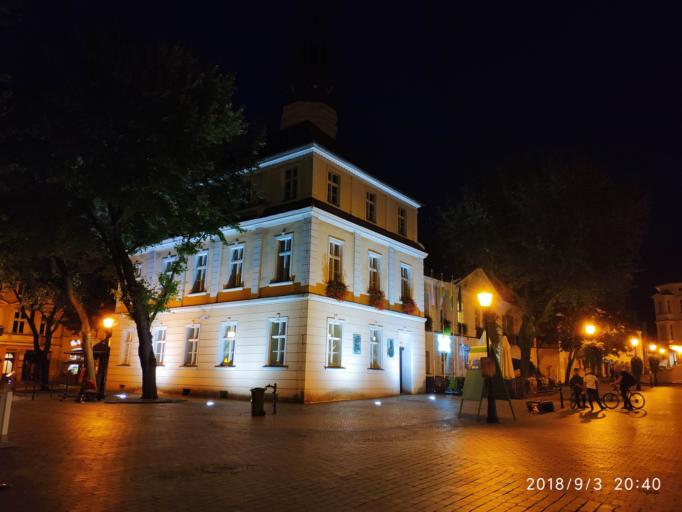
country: PL
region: Lubusz
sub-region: Zielona Gora
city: Zielona Gora
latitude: 51.9387
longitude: 15.5049
